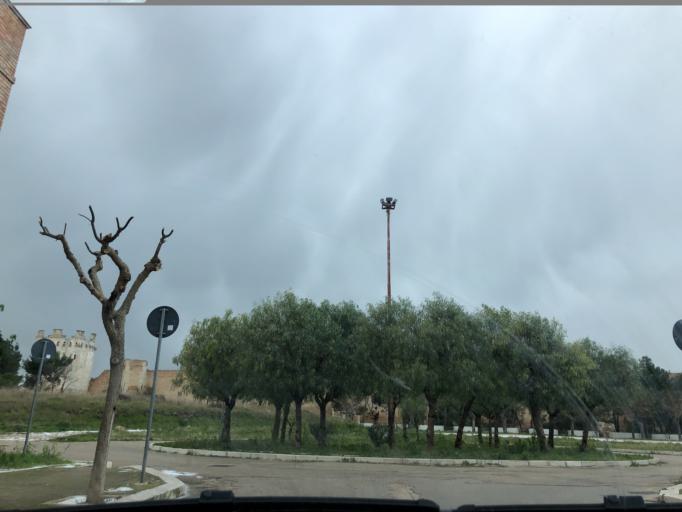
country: IT
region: Apulia
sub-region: Provincia di Foggia
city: Lucera
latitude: 41.5084
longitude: 15.3245
